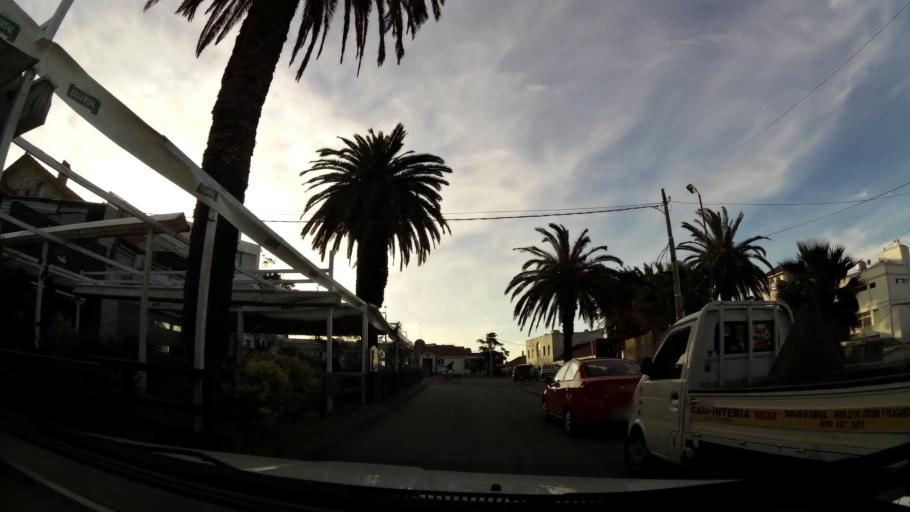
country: UY
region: Maldonado
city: Punta del Este
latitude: -34.9652
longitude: -54.9501
